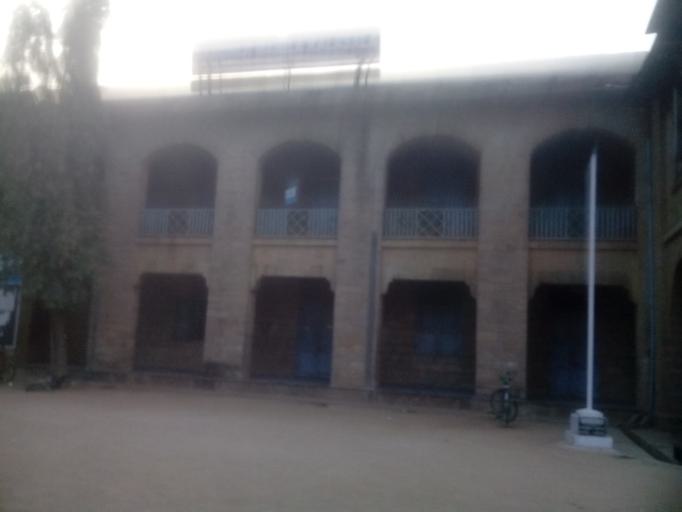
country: IN
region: Andhra Pradesh
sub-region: Krishna
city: Vijayawada
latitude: 16.5148
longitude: 80.6131
